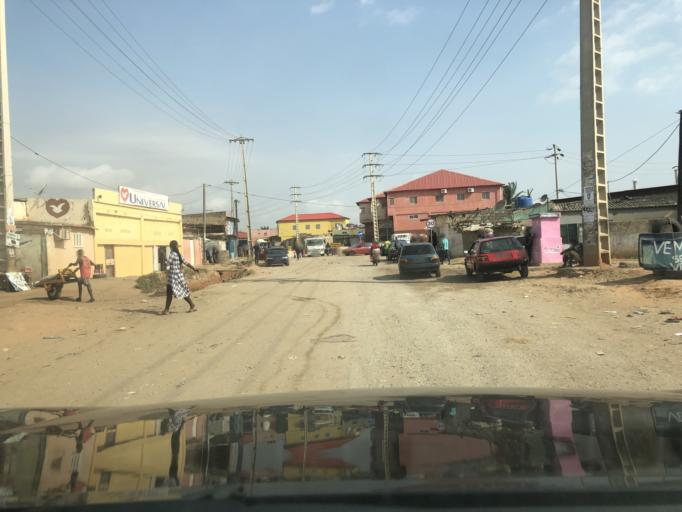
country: AO
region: Luanda
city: Luanda
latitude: -8.8516
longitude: 13.2570
